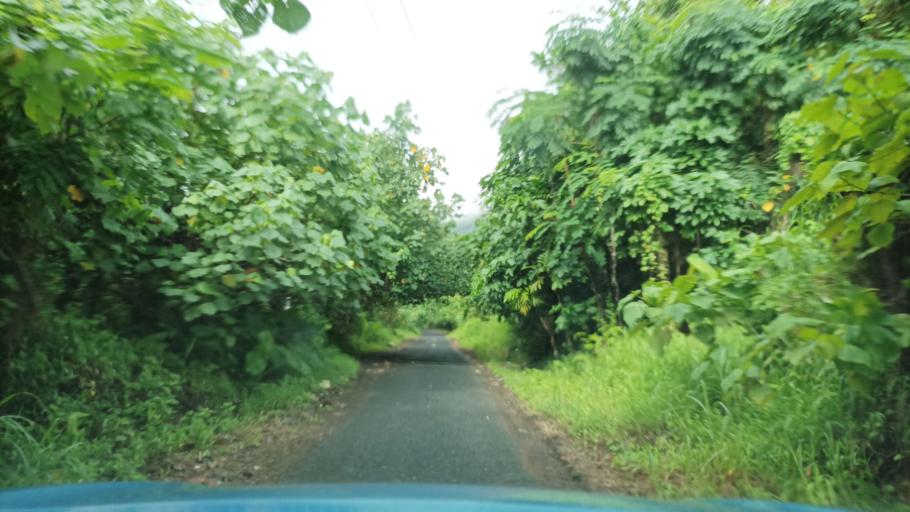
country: FM
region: Pohnpei
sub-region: Kolonia Municipality
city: Kolonia
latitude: 6.9240
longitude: 158.2850
